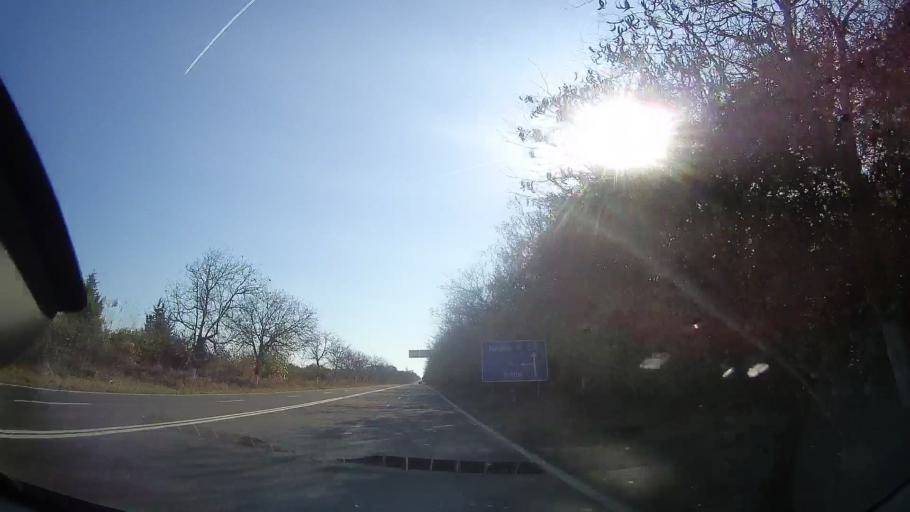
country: RO
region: Constanta
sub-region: Comuna Douazeci si Trei August
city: Dulcesti
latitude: 43.8821
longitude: 28.5733
